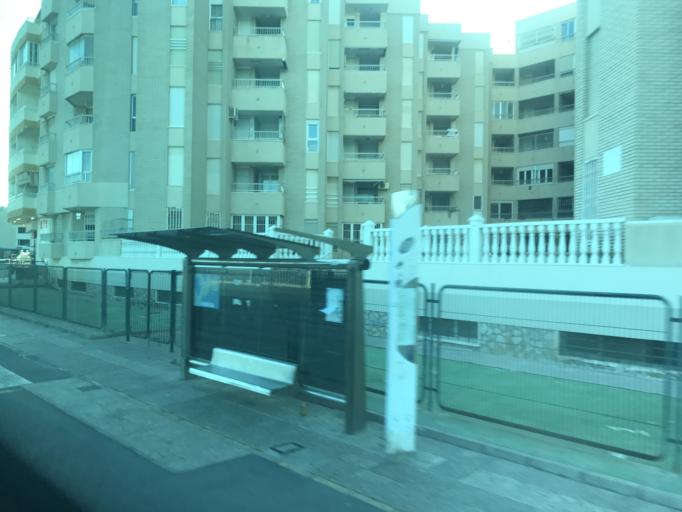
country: ES
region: Valencia
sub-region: Provincia de Alicante
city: Torrevieja
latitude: 37.9812
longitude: -0.6630
